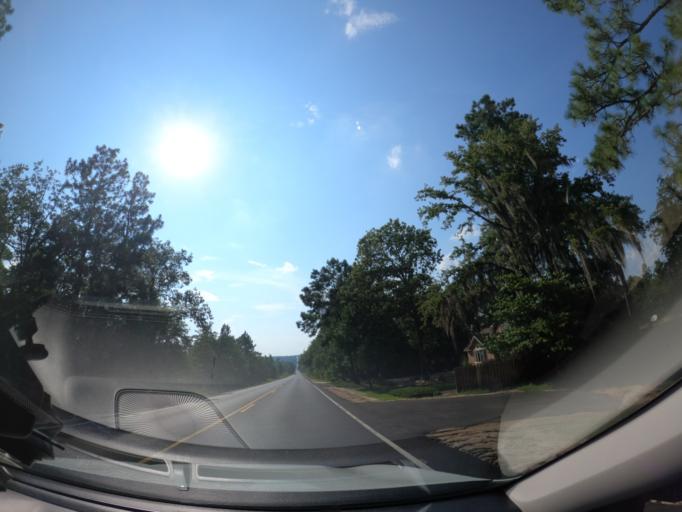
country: US
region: South Carolina
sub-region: Aiken County
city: Jackson
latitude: 33.4045
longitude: -81.7761
